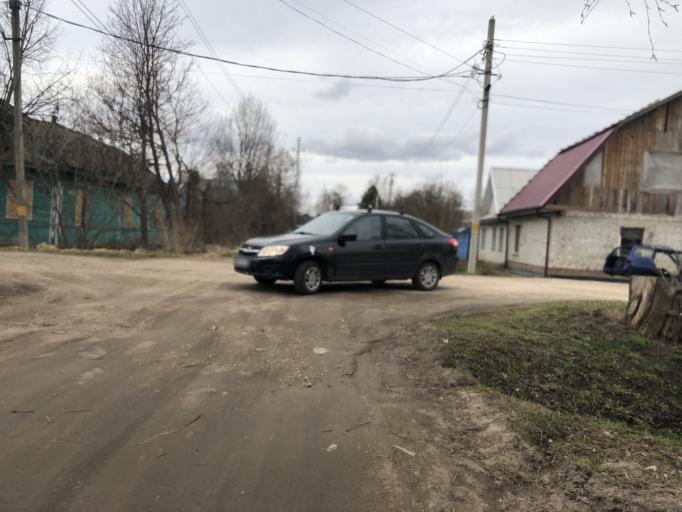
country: RU
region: Tverskaya
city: Rzhev
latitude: 56.2500
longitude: 34.3170
